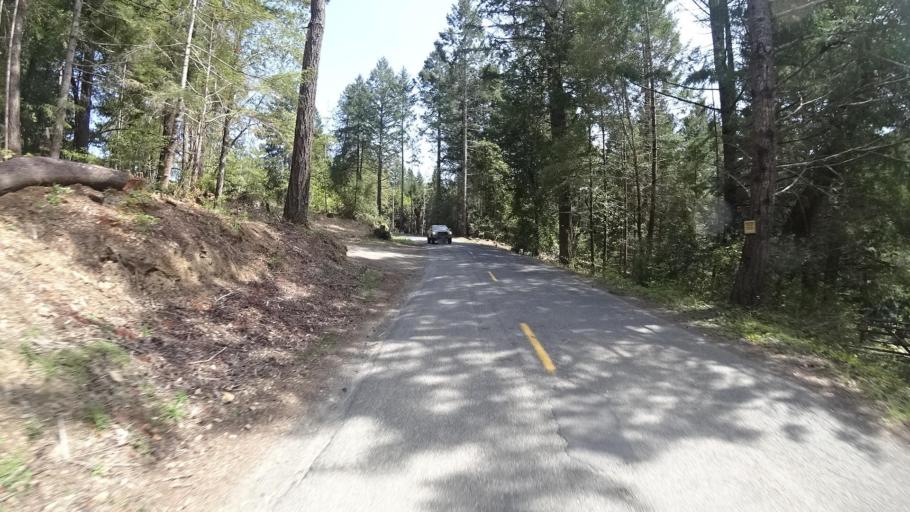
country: US
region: California
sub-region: Humboldt County
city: Redway
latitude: 40.3568
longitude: -123.7226
